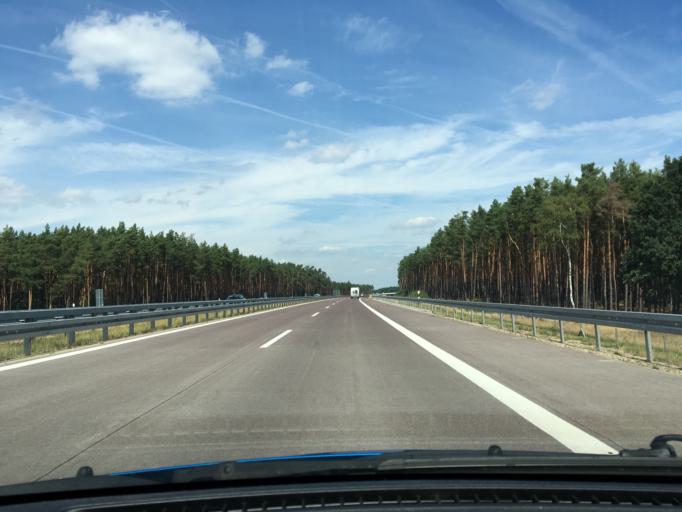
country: DE
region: Mecklenburg-Vorpommern
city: Ludwigslust
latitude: 53.3490
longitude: 11.5175
